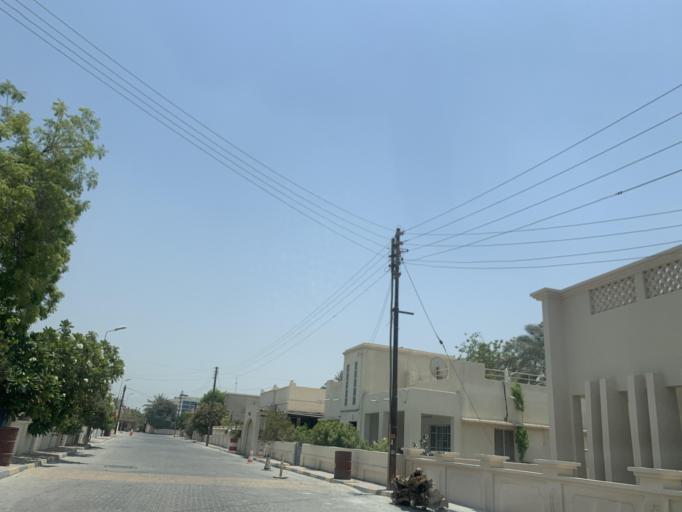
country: BH
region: Manama
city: Jidd Hafs
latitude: 26.2193
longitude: 50.5617
